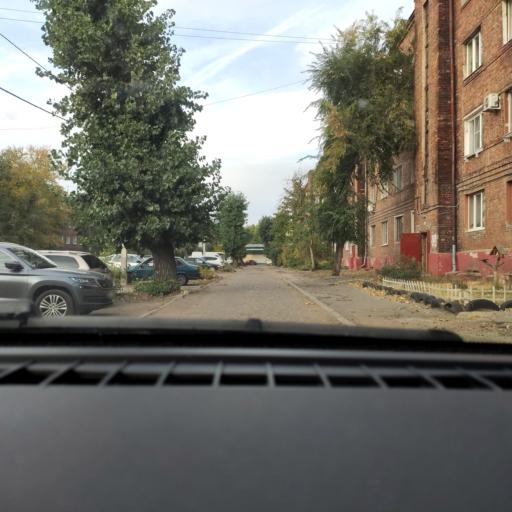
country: RU
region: Voronezj
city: Voronezh
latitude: 51.6386
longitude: 39.2429
